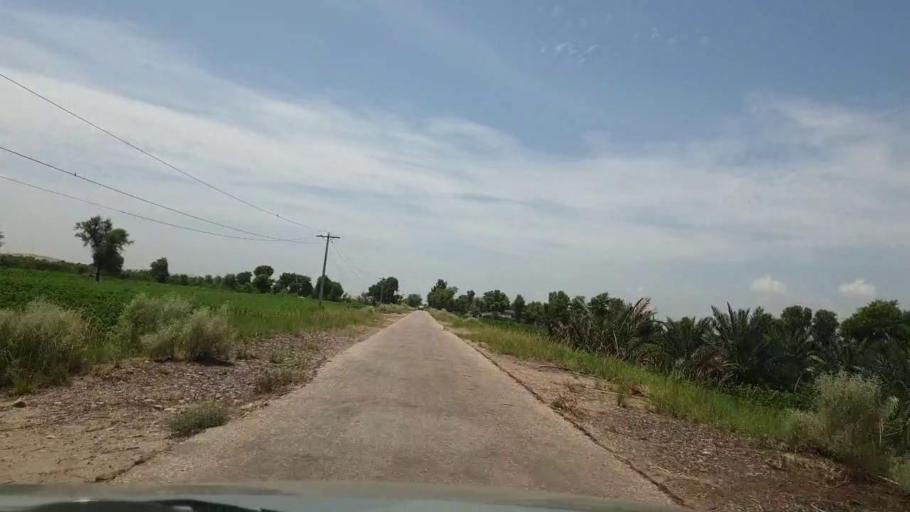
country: PK
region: Sindh
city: Bozdar
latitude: 27.0562
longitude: 68.9806
